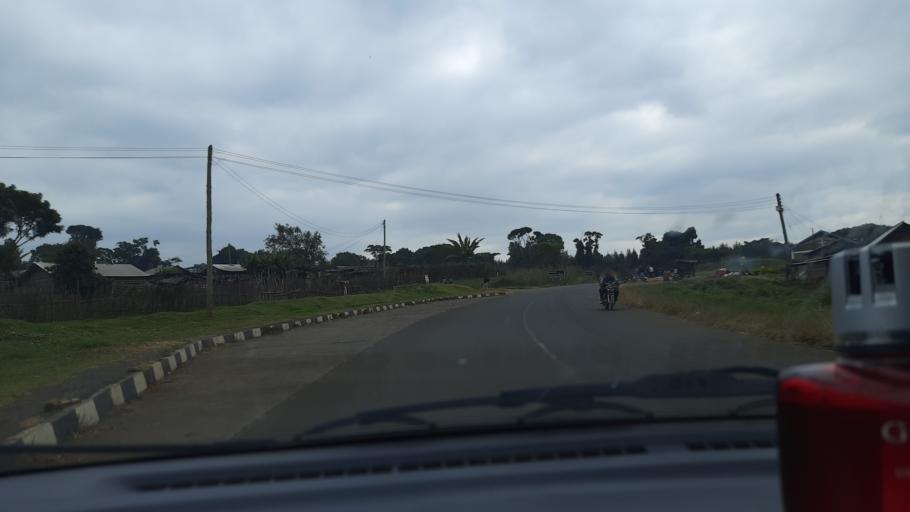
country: TZ
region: Kilimanjaro
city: Moshi
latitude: -2.9569
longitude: 37.4999
